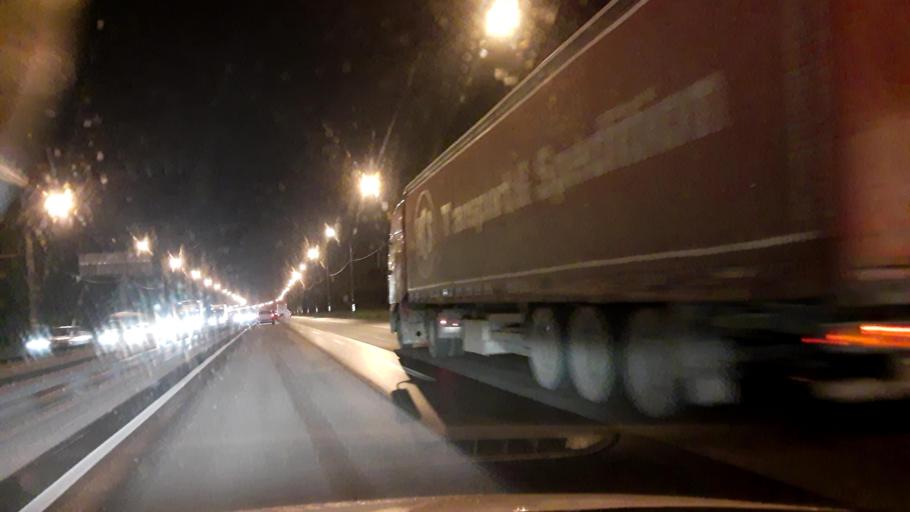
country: RU
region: Moskovskaya
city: Monino
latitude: 55.8262
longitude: 38.2258
